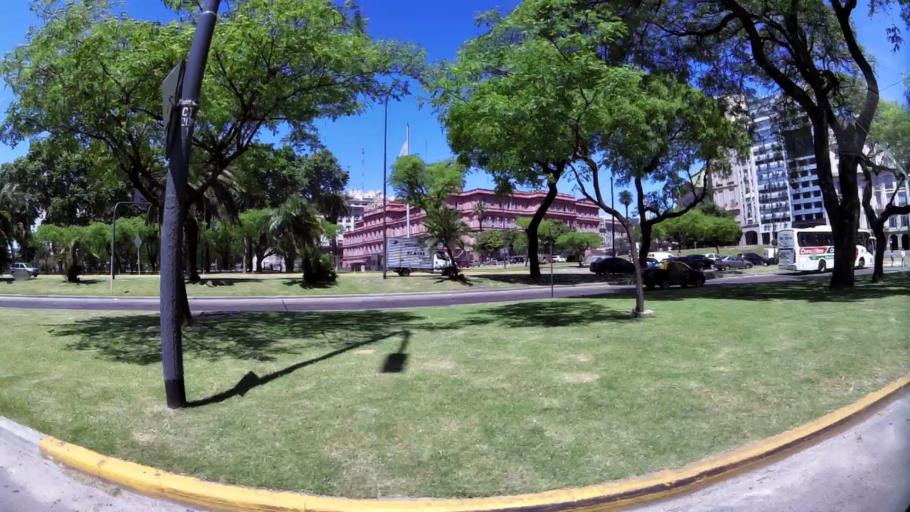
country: AR
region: Buenos Aires F.D.
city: Buenos Aires
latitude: -34.6067
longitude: -58.3692
